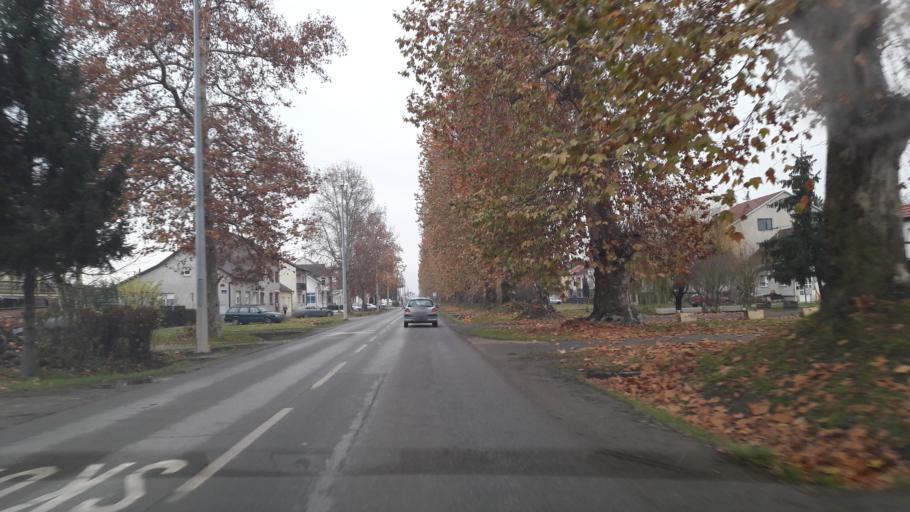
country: HR
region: Osjecko-Baranjska
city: Visnjevac
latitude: 45.5698
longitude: 18.6106
